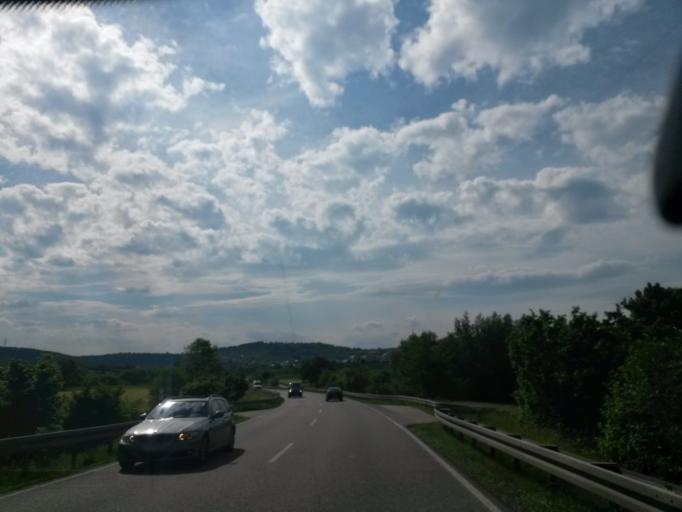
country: DE
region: Baden-Wuerttemberg
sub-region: Karlsruhe Region
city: Simmozheim
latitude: 48.7486
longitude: 8.8333
